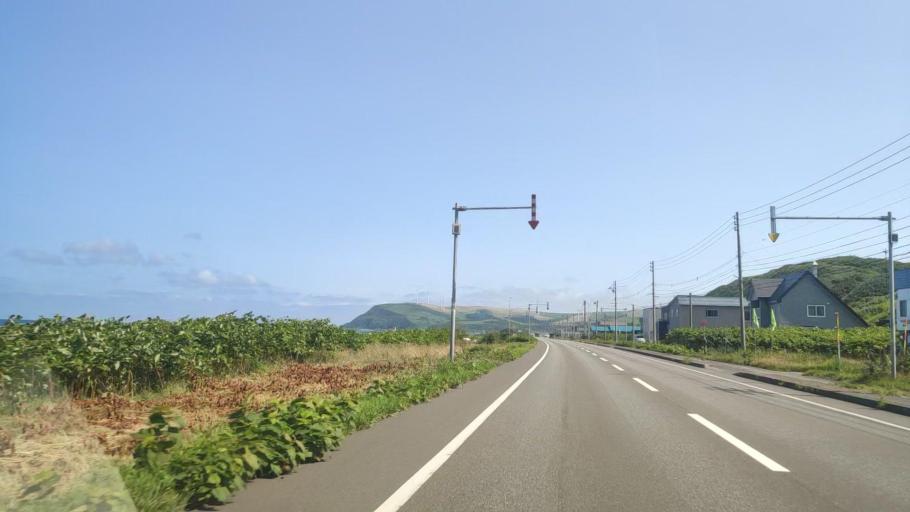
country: JP
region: Hokkaido
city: Makubetsu
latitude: 45.4428
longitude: 141.8666
